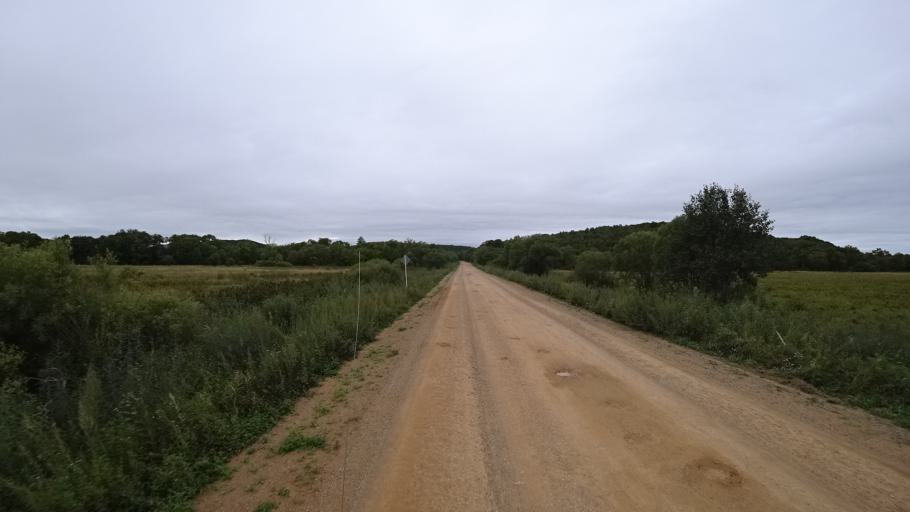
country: RU
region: Primorskiy
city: Rettikhovka
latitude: 44.1744
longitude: 132.8778
